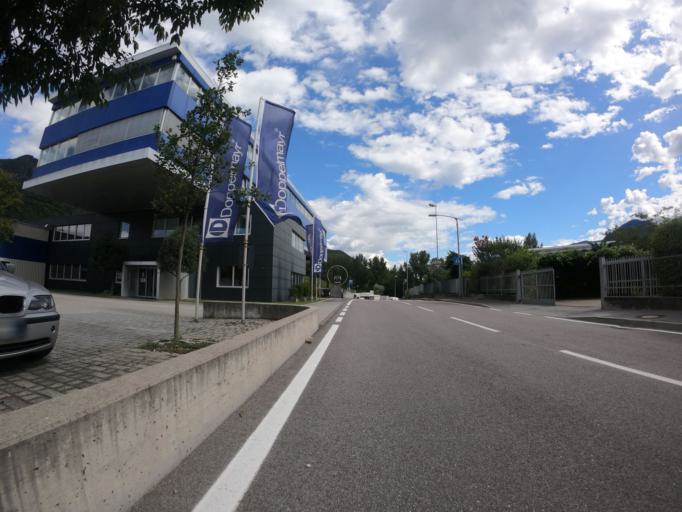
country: IT
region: Trentino-Alto Adige
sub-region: Bolzano
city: Sinigo
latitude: 46.6298
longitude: 11.1716
